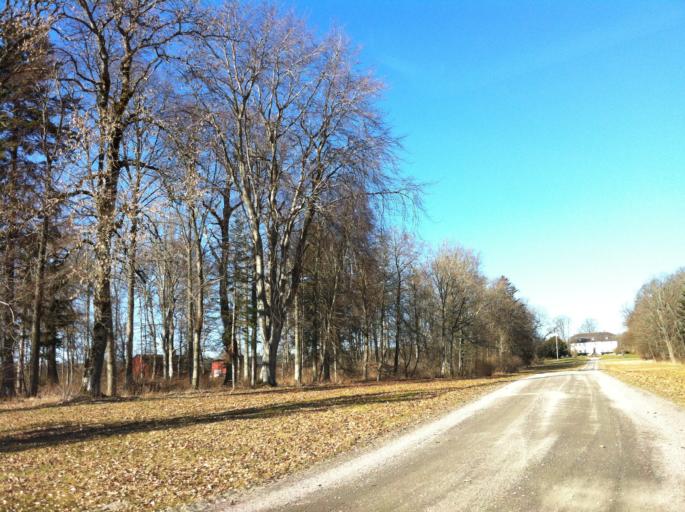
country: SE
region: Vaestra Goetaland
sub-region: Grastorps Kommun
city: Graestorp
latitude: 58.4471
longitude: 12.6166
